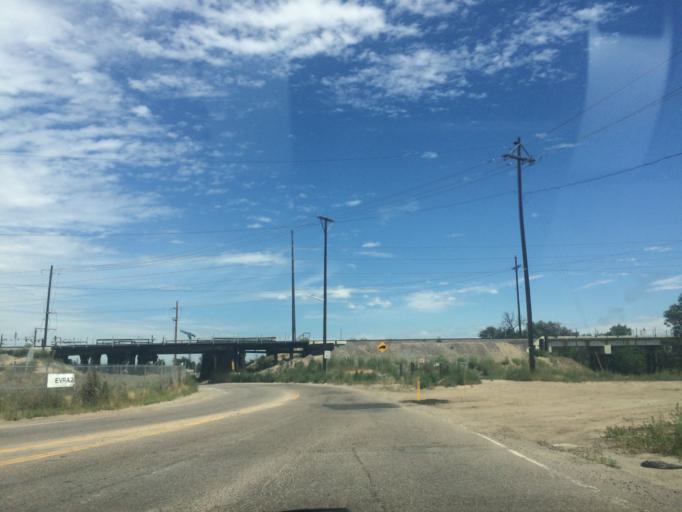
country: US
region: Colorado
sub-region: Adams County
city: Commerce City
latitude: 39.8021
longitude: -104.9597
